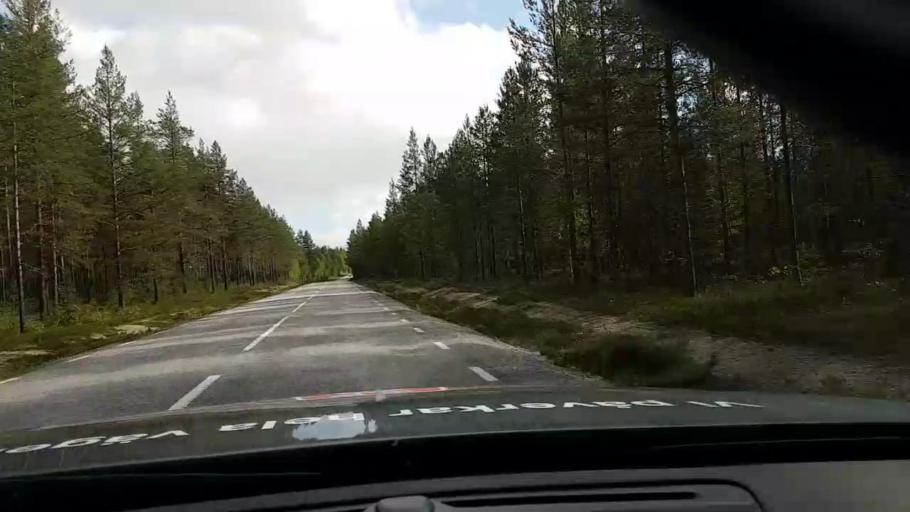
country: SE
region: Vaesternorrland
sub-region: OErnskoeldsviks Kommun
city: Bredbyn
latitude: 63.6524
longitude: 17.8875
